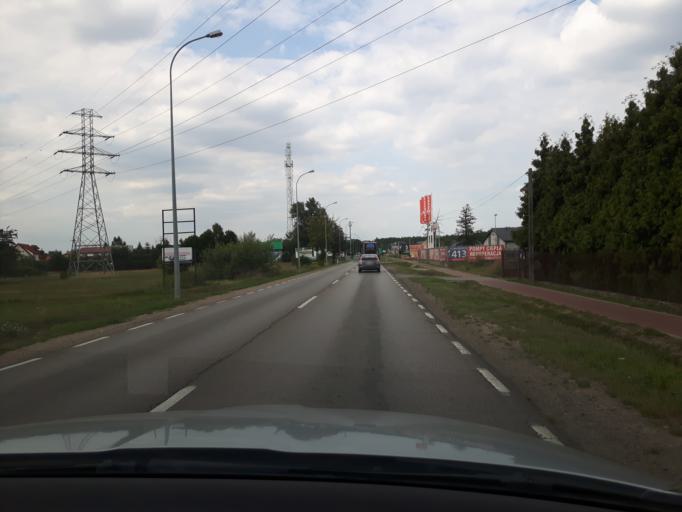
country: PL
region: Masovian Voivodeship
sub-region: Powiat legionowski
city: Stanislawow Pierwszy
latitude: 52.3741
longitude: 21.0291
